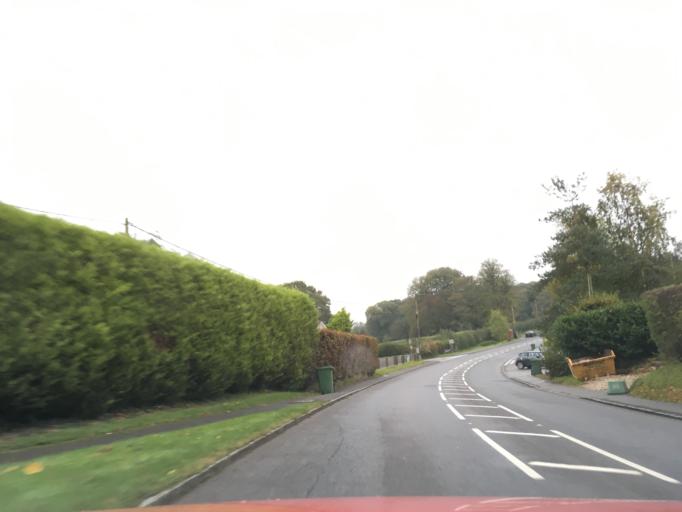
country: GB
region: England
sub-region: West Berkshire
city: Wickham
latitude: 51.4440
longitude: -1.4337
